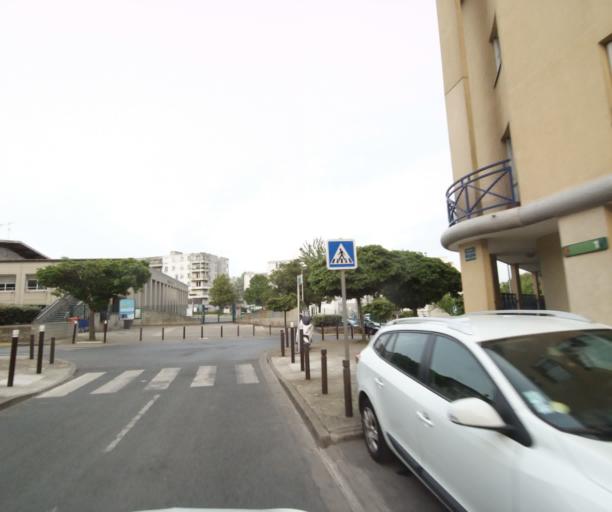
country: FR
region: Ile-de-France
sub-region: Departement de Seine-et-Marne
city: Torcy
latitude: 48.8444
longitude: 2.6451
